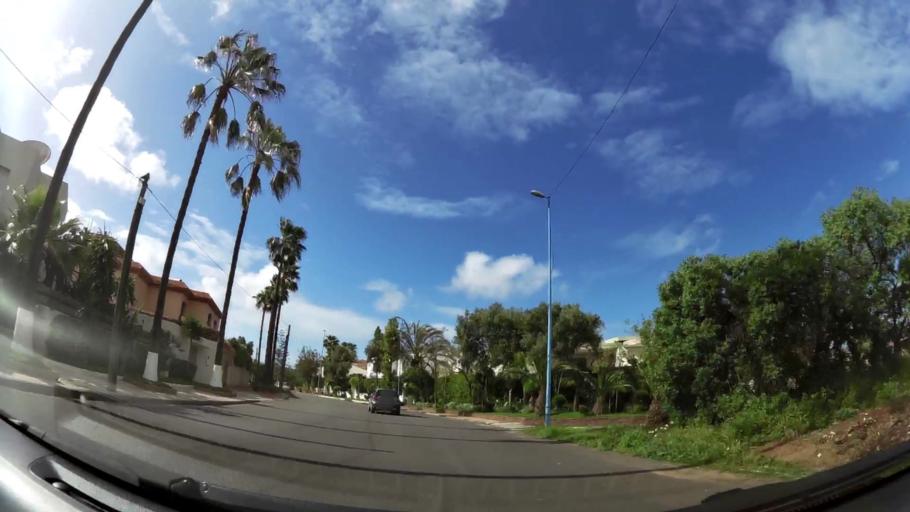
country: MA
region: Grand Casablanca
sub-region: Casablanca
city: Casablanca
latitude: 33.5458
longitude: -7.6266
